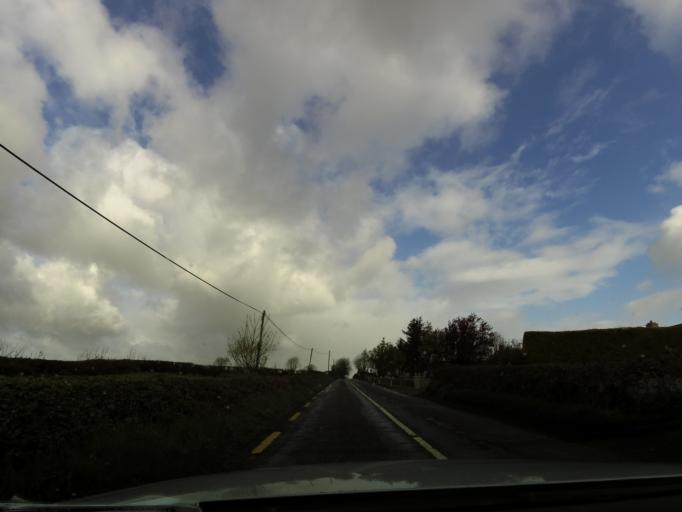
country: IE
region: Munster
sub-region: North Tipperary
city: Nenagh
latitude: 52.8433
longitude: -8.1436
